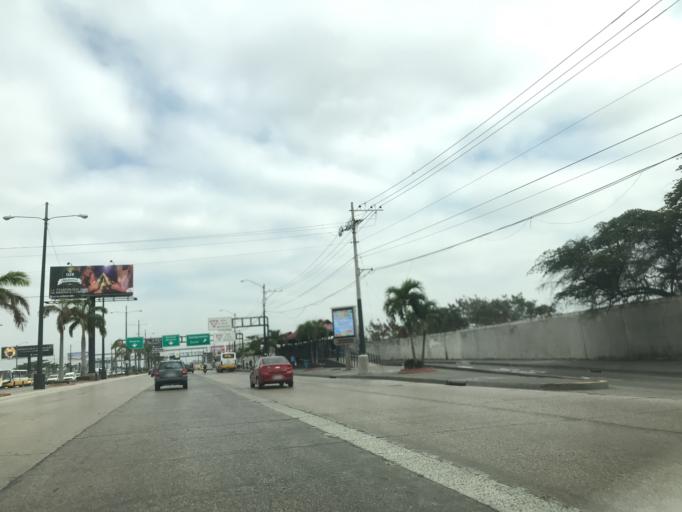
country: EC
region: Guayas
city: Eloy Alfaro
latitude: -2.1628
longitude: -79.8801
